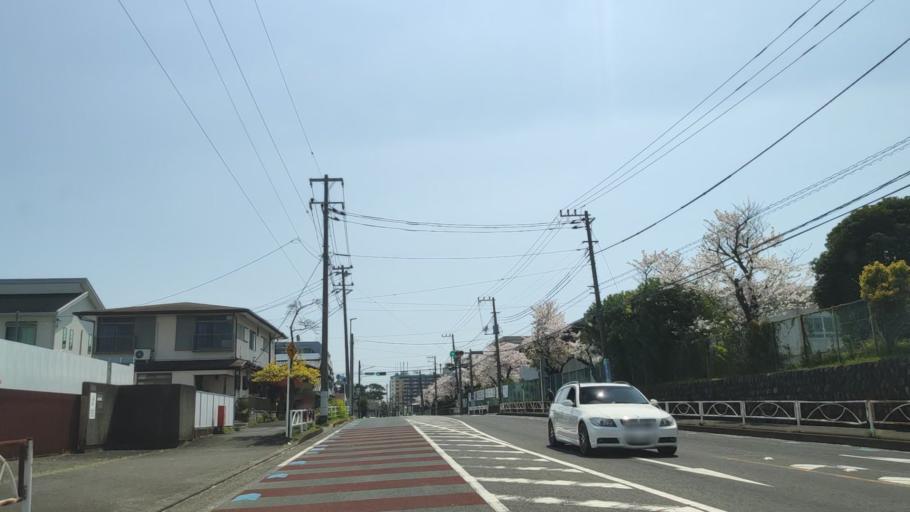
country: JP
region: Kanagawa
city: Hiratsuka
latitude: 35.3234
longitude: 139.3382
